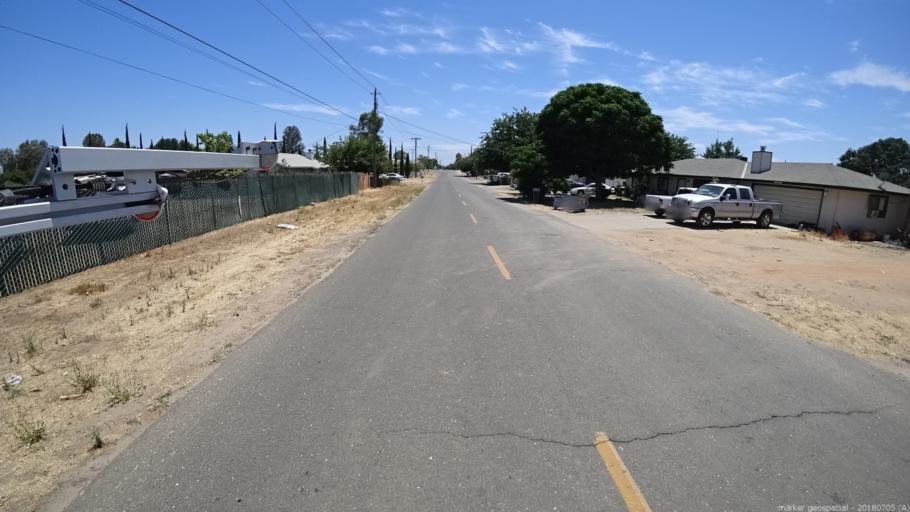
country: US
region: California
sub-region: Madera County
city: Madera
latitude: 36.9927
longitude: -120.0370
